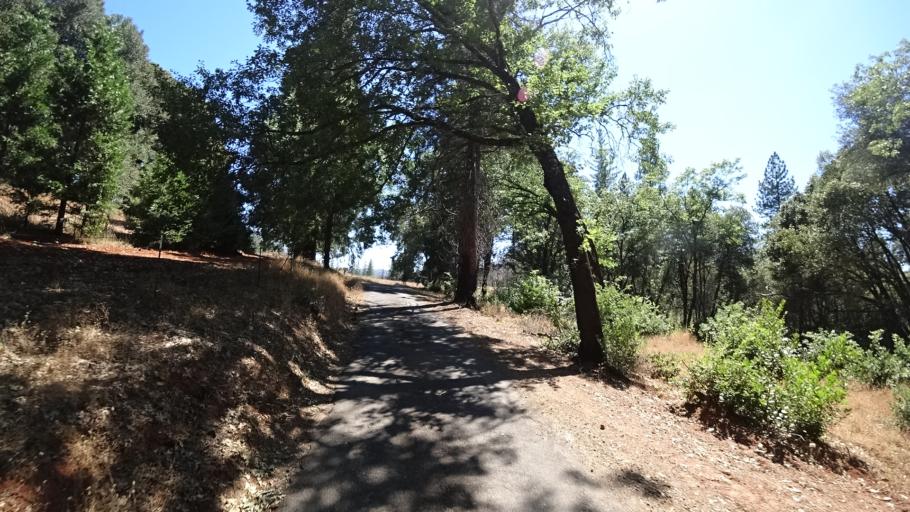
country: US
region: California
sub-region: Calaveras County
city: Mountain Ranch
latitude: 38.2782
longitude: -120.5816
